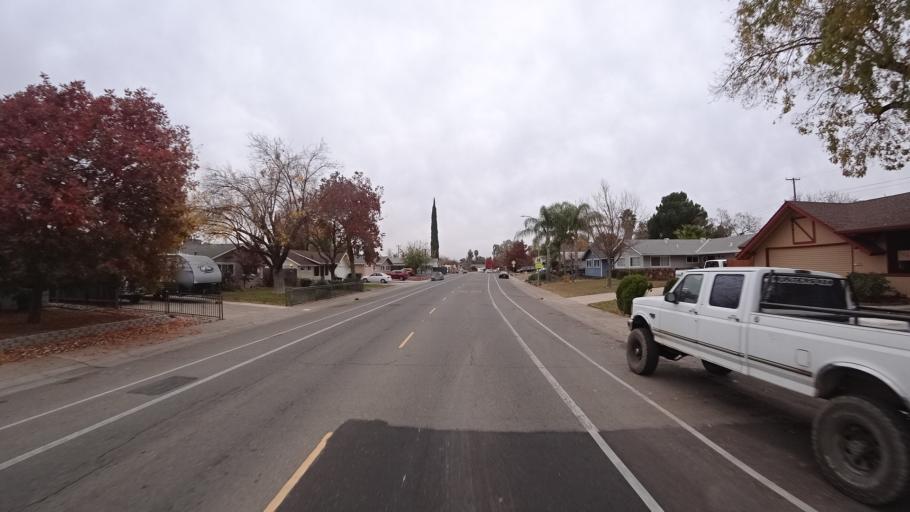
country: US
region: California
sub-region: Sacramento County
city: Citrus Heights
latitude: 38.6949
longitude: -121.2945
